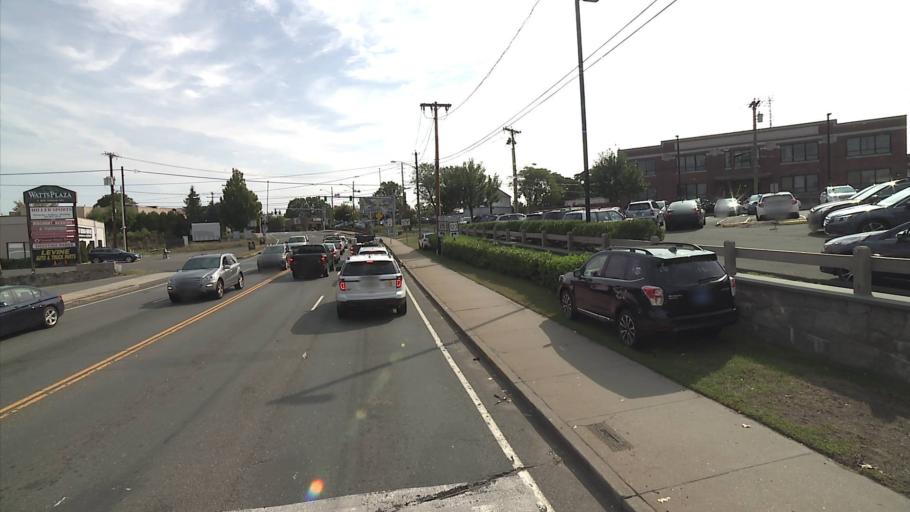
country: US
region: Connecticut
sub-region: Fairfield County
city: Norwalk
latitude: 41.1265
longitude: -73.4234
